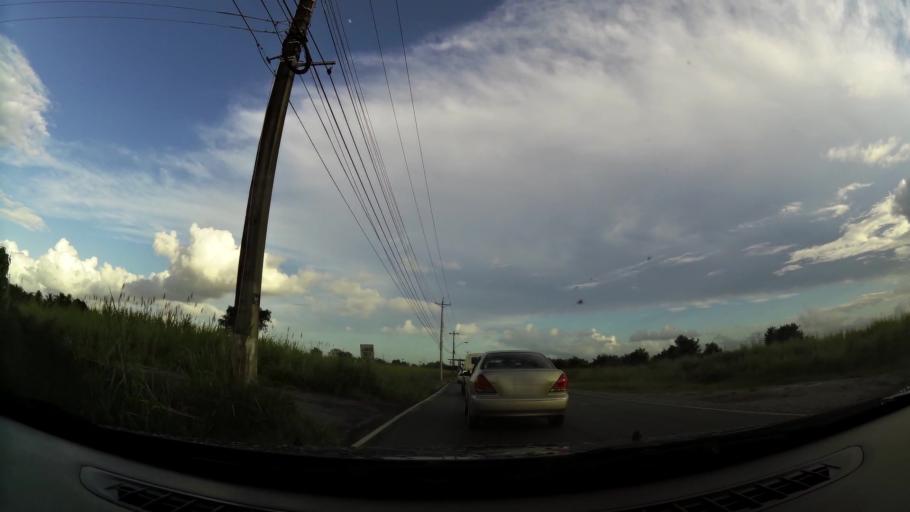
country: TT
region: Tunapuna/Piarco
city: Tunapuna
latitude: 10.5976
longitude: -61.3699
